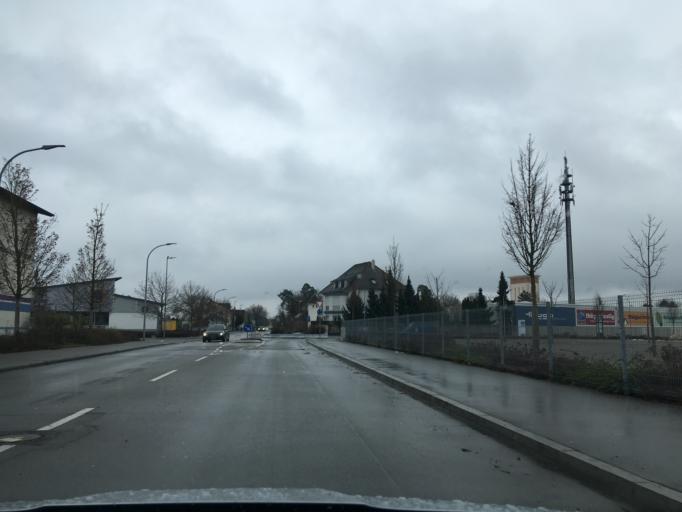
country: DE
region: Baden-Wuerttemberg
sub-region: Freiburg Region
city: Singen
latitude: 47.7510
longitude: 8.8501
